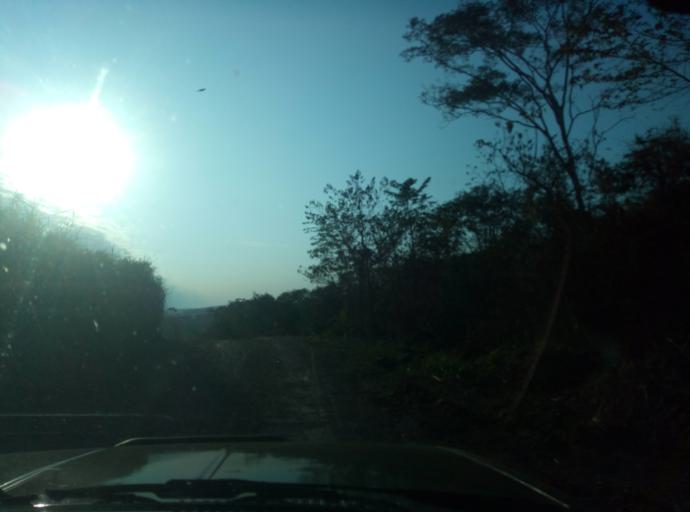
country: PY
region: Caaguazu
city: Doctor Cecilio Baez
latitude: -25.1987
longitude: -56.1329
